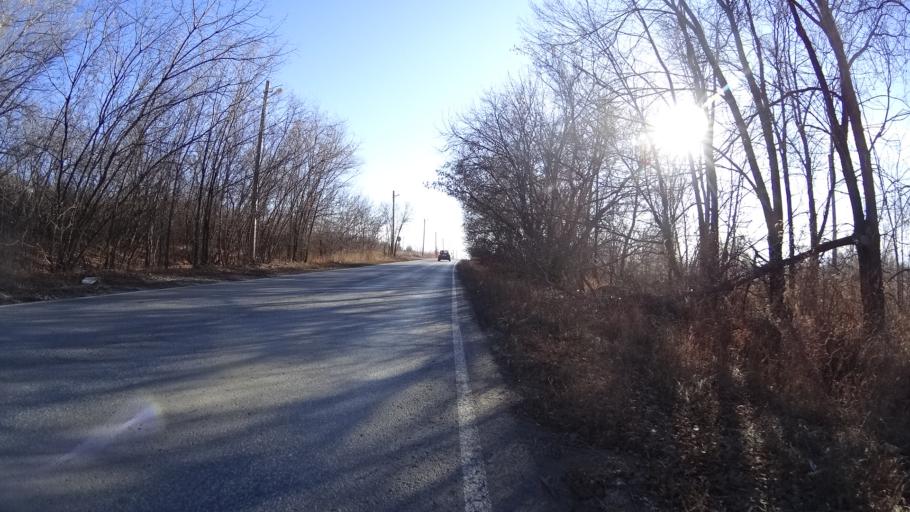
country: RU
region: Chelyabinsk
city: Troitsk
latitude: 54.0469
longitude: 61.6213
